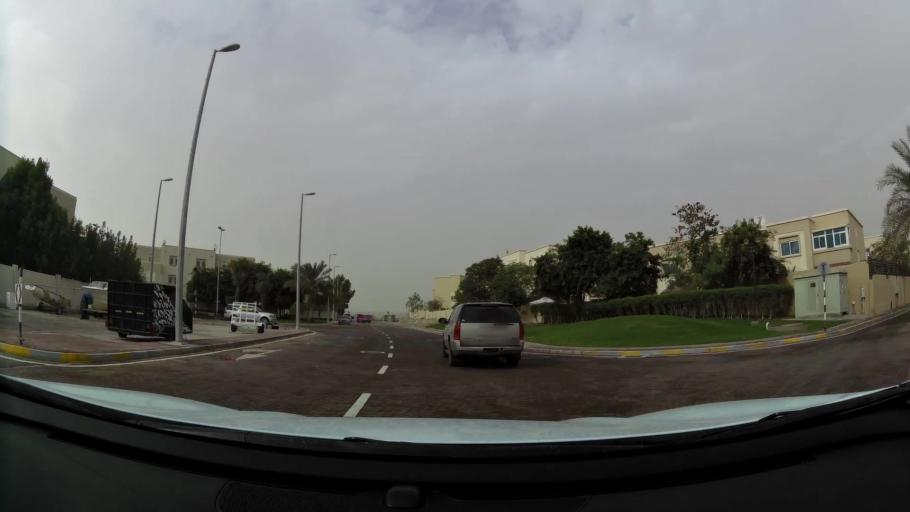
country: AE
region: Abu Dhabi
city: Abu Dhabi
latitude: 24.4558
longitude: 54.6694
